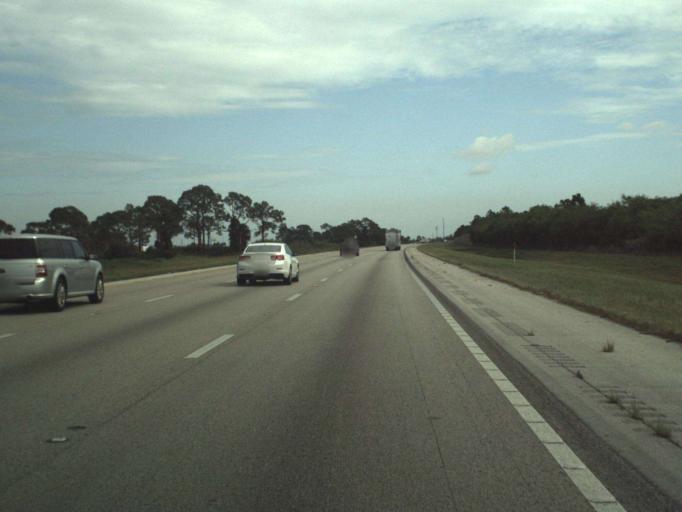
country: US
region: Florida
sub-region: Saint Lucie County
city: Port Saint Lucie
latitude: 27.1808
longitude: -80.3967
